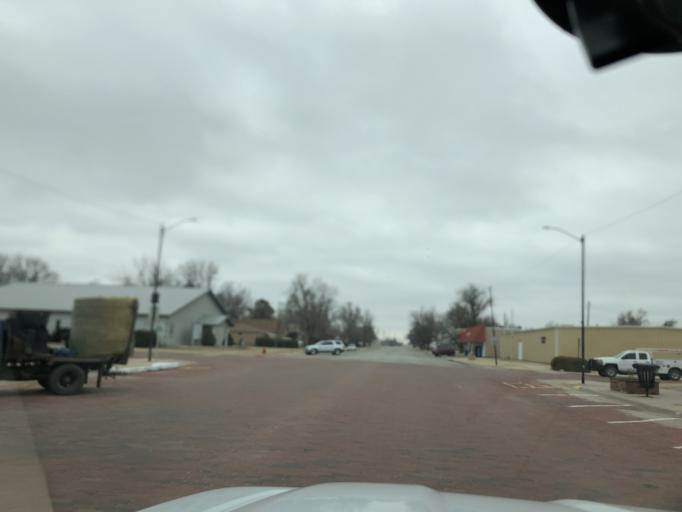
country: US
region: Kansas
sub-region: Stafford County
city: Stafford
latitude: 37.9602
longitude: -98.6004
